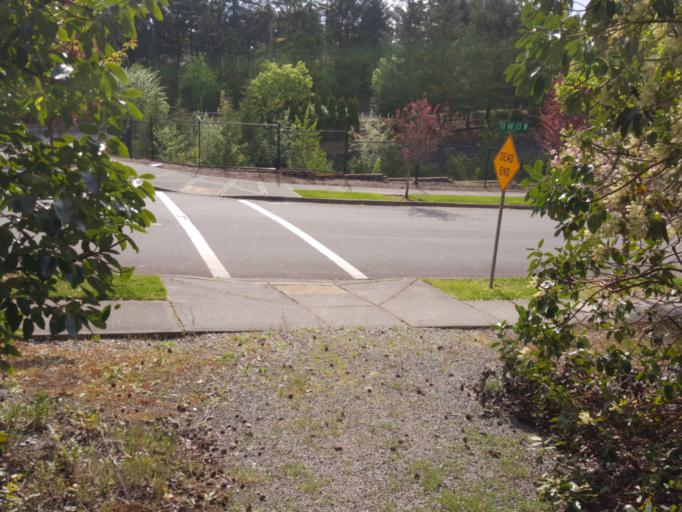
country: US
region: Washington
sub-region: Pierce County
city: University Place
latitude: 47.2124
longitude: -122.5308
